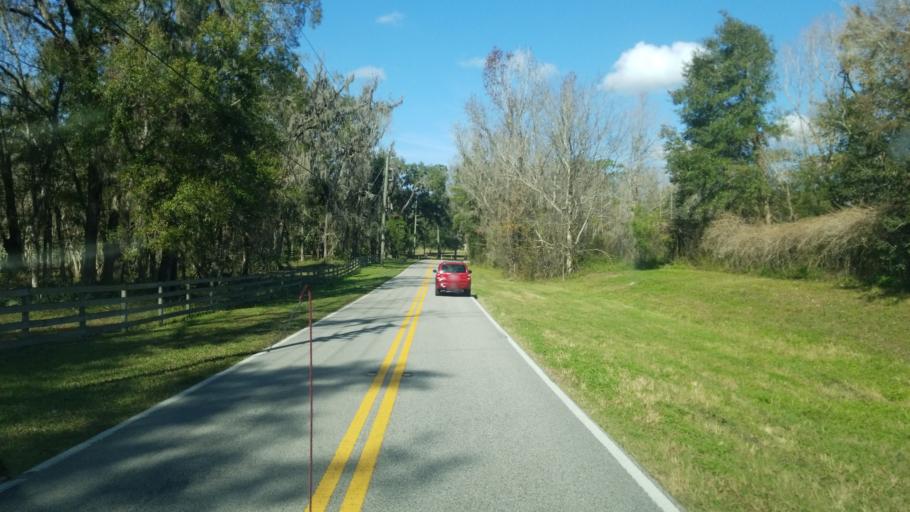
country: US
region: Florida
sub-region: Hernando County
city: North Brooksville
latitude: 28.5917
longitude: -82.3750
